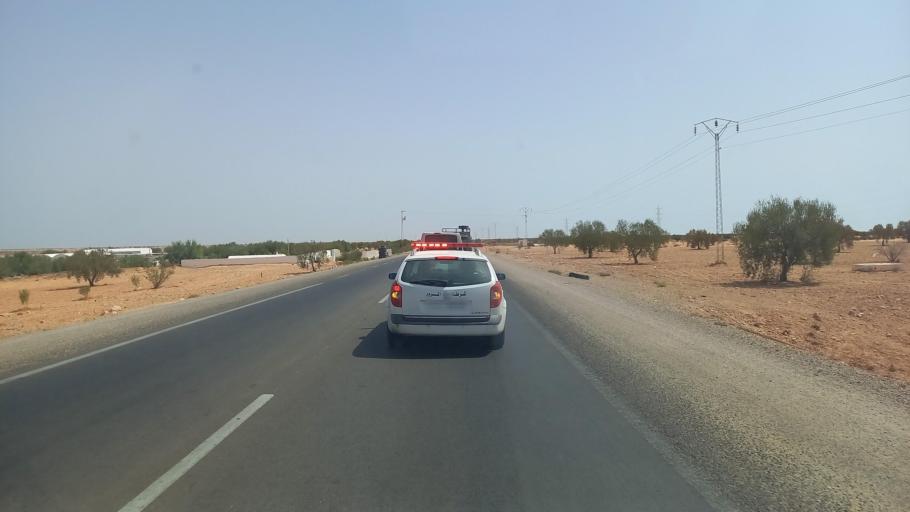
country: TN
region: Madanin
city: Zarzis
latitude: 33.3995
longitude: 10.8332
